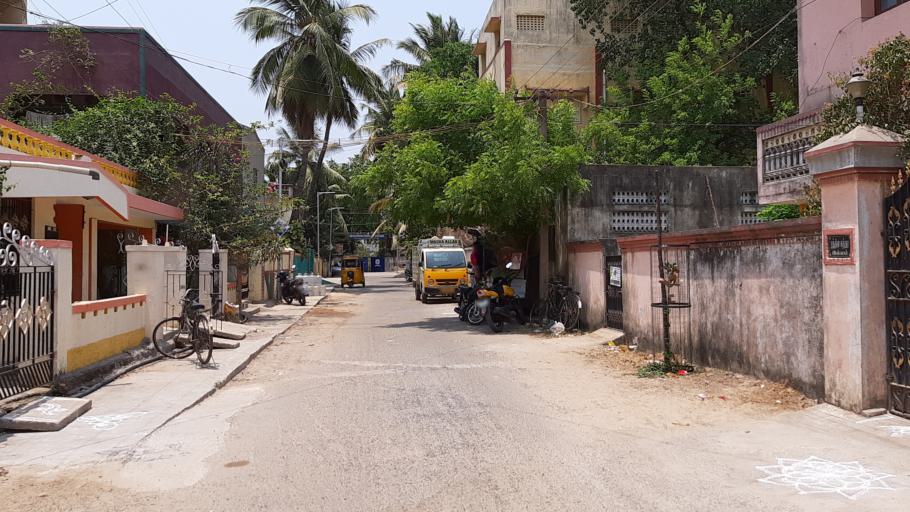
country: IN
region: Tamil Nadu
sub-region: Kancheepuram
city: Manappakkam
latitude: 13.0281
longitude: 80.1869
